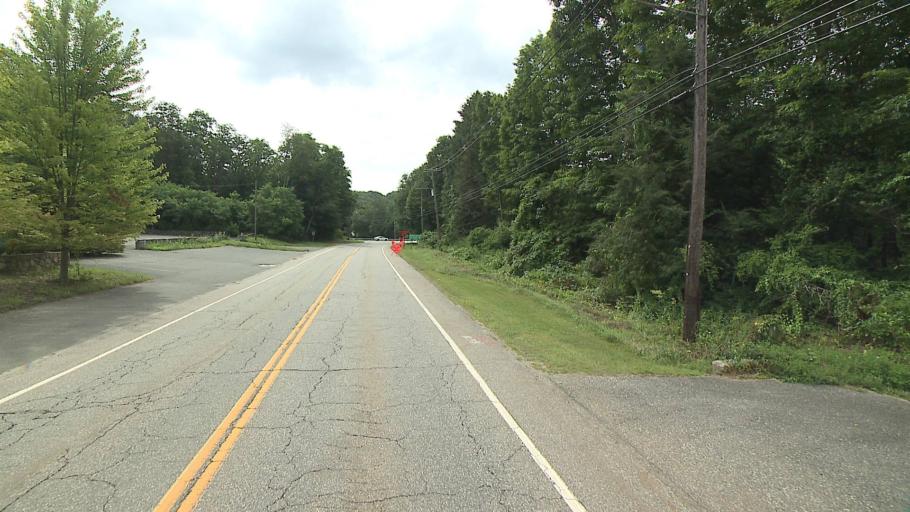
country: US
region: Connecticut
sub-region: Litchfield County
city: New Preston
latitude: 41.6453
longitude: -73.3173
